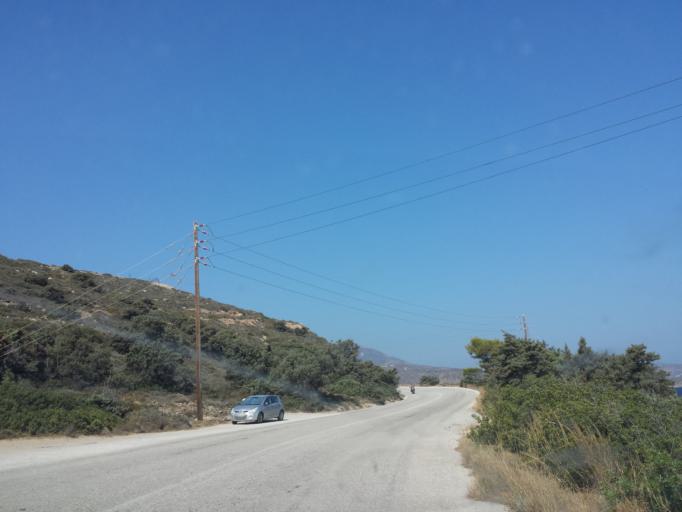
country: GR
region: South Aegean
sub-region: Nomos Kykladon
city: Adamas
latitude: 36.6916
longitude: 24.4554
